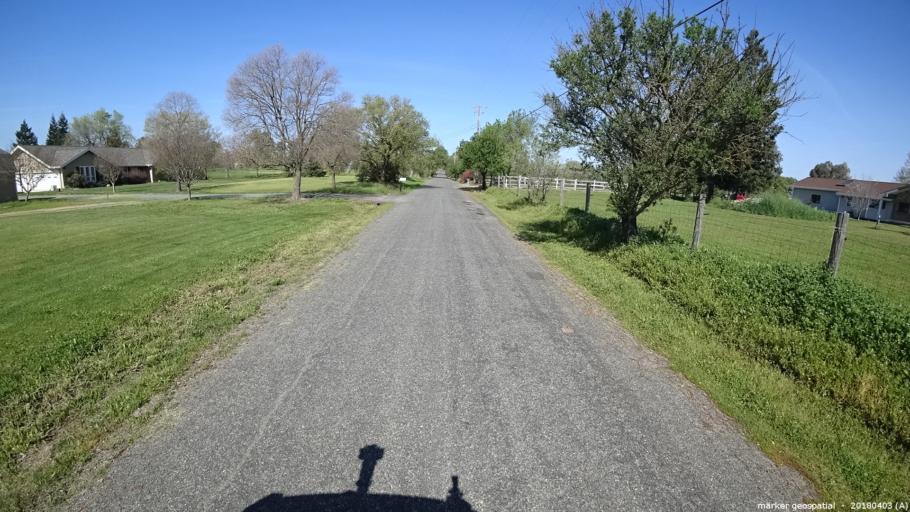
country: US
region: California
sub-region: Sacramento County
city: Wilton
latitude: 38.4274
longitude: -121.2182
